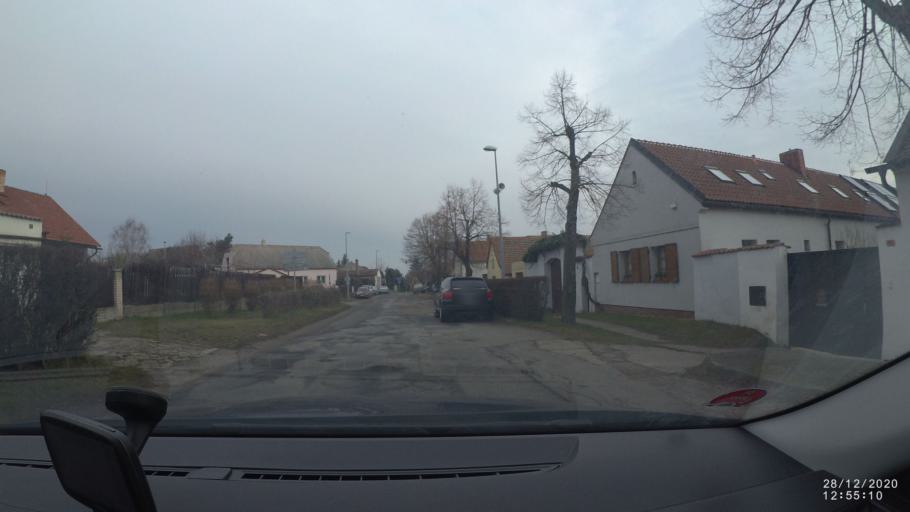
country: CZ
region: Praha
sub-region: Praha 19
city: Satalice
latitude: 50.1552
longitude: 14.5775
